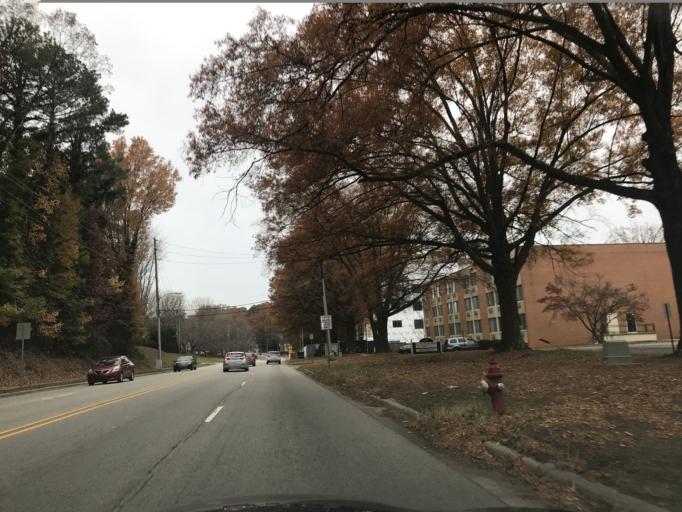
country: US
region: North Carolina
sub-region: Wake County
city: West Raleigh
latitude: 35.7966
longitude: -78.6500
